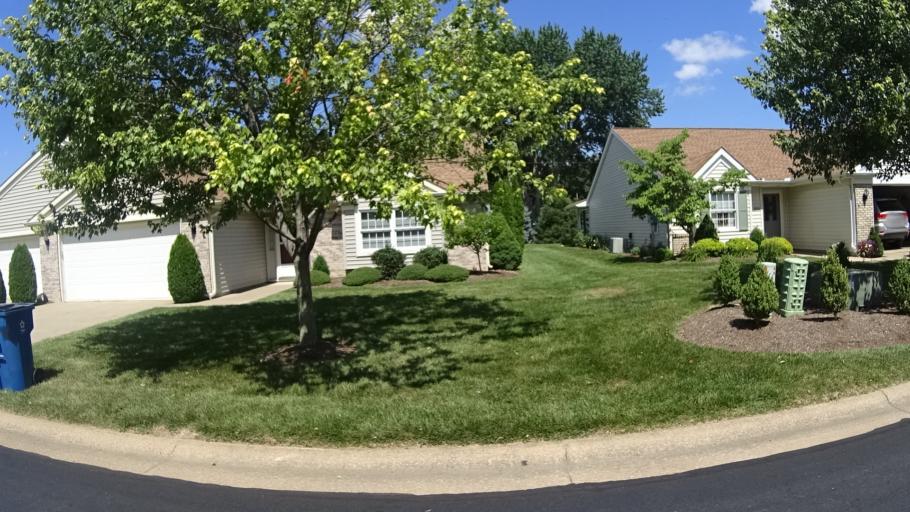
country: US
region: Ohio
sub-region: Erie County
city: Huron
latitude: 41.3835
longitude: -82.5647
